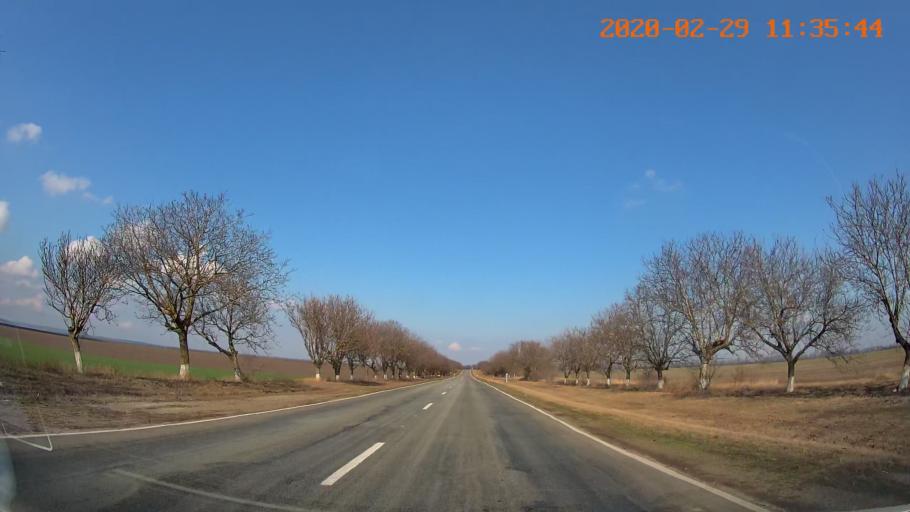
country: MD
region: Rezina
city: Saharna
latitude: 47.5850
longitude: 29.0614
